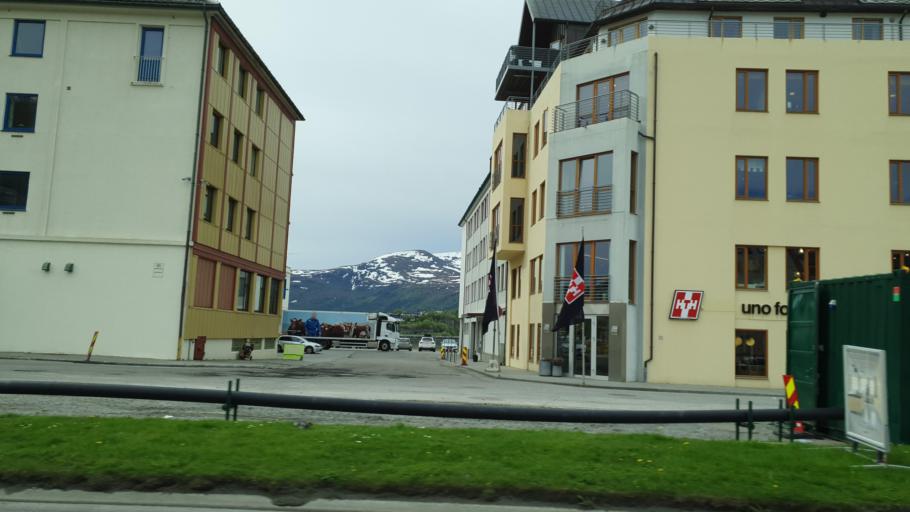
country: NO
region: More og Romsdal
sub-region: Alesund
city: Alesund
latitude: 62.4708
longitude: 6.1641
